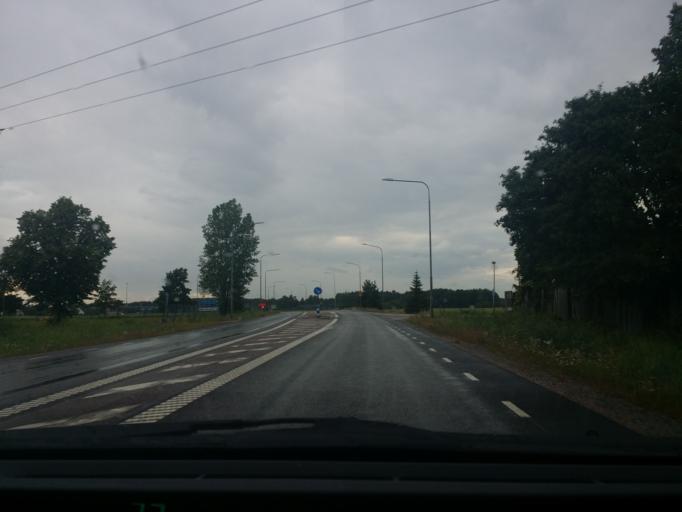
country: SE
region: Vaestmanland
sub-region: Arboga Kommun
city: Arboga
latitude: 59.4046
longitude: 15.8549
